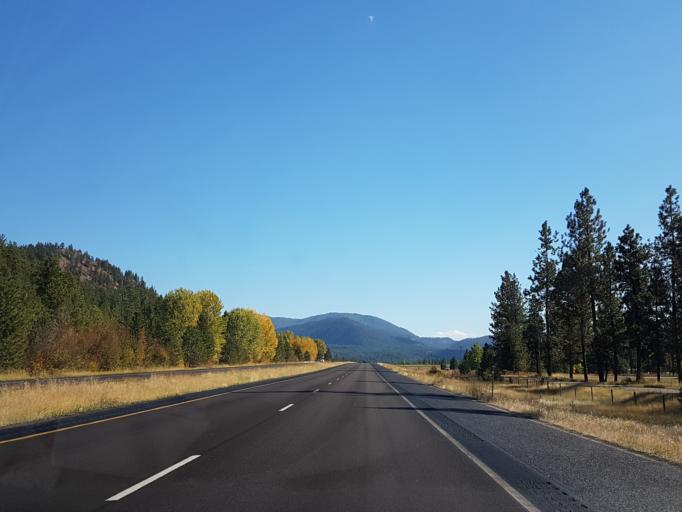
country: US
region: Montana
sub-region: Mineral County
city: Superior
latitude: 47.1450
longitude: -114.8178
